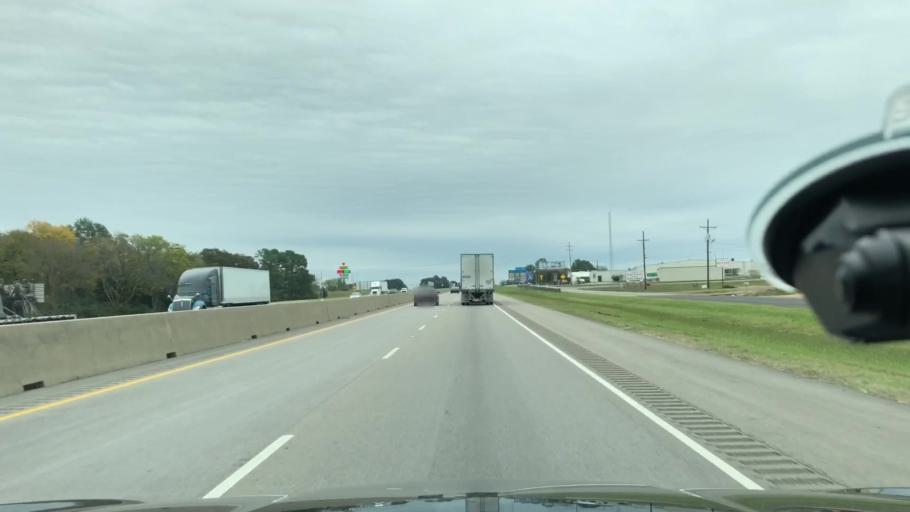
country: US
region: Texas
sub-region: Franklin County
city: Mount Vernon
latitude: 33.1620
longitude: -95.2272
